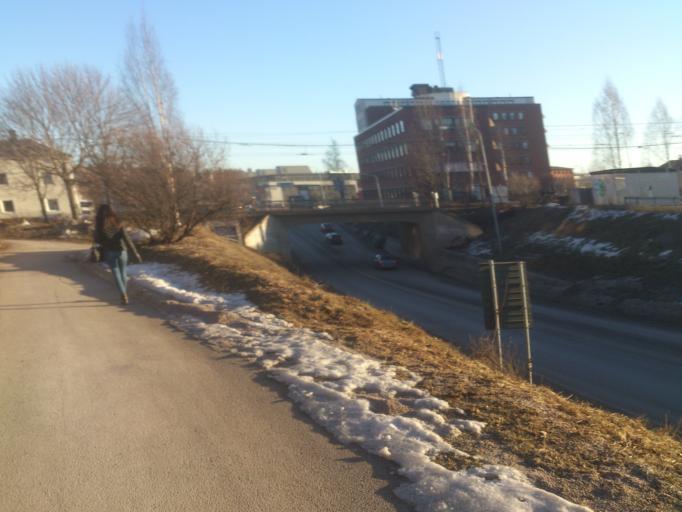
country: SE
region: Vaesternorrland
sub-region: Sundsvalls Kommun
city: Sundsvall
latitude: 62.3866
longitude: 17.3121
